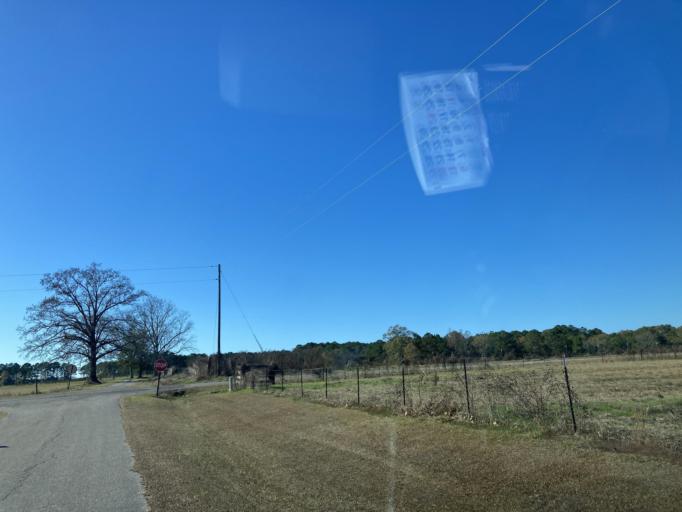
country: US
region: Mississippi
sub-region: Lamar County
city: Sumrall
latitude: 31.3197
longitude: -89.6492
